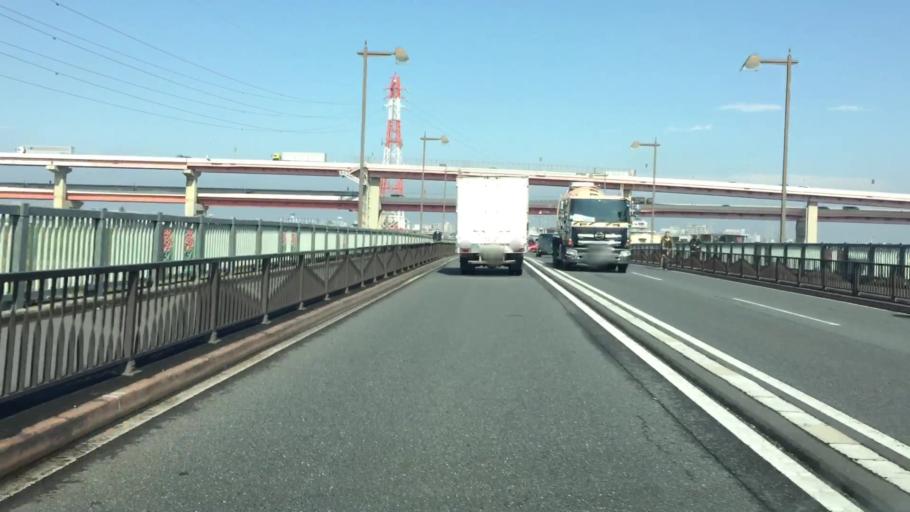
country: JP
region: Saitama
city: Soka
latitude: 35.7584
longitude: 139.7893
